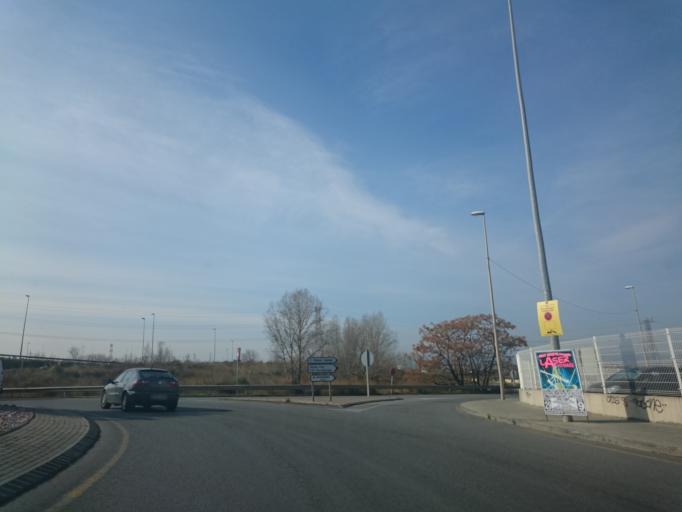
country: ES
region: Catalonia
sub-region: Provincia de Barcelona
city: L'Hospitalet de Llobregat
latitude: 41.3434
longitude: 2.1046
